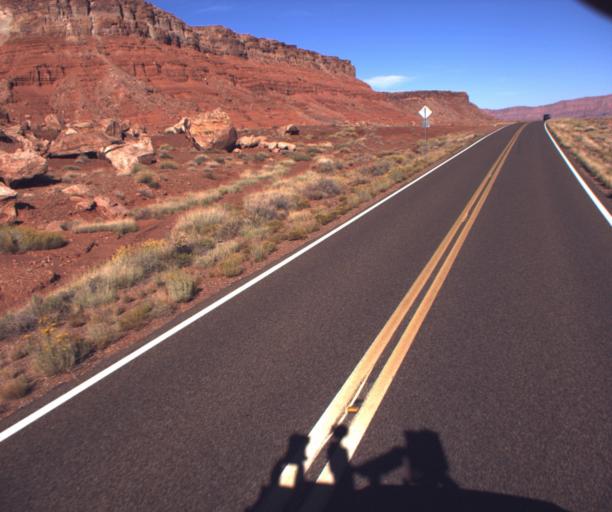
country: US
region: Arizona
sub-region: Coconino County
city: Page
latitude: 36.7470
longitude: -111.7424
